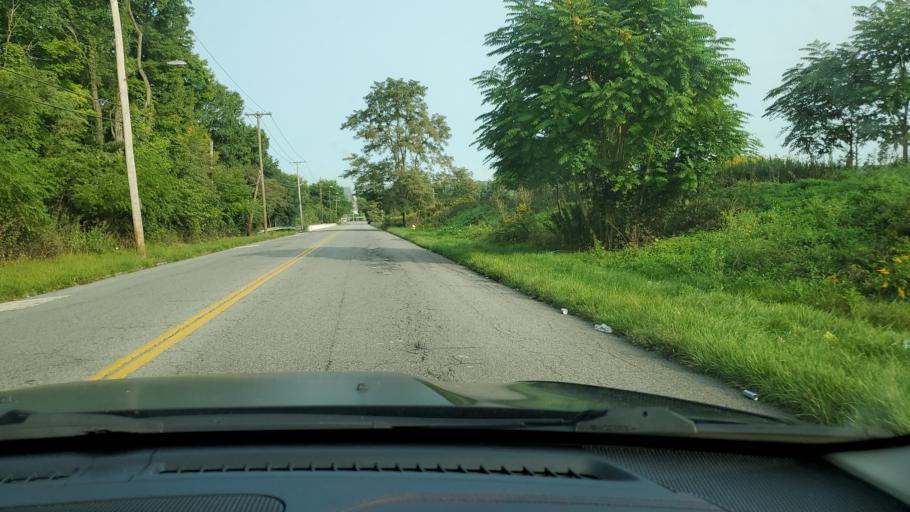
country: US
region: Ohio
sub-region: Mahoning County
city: Campbell
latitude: 41.0723
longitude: -80.6216
